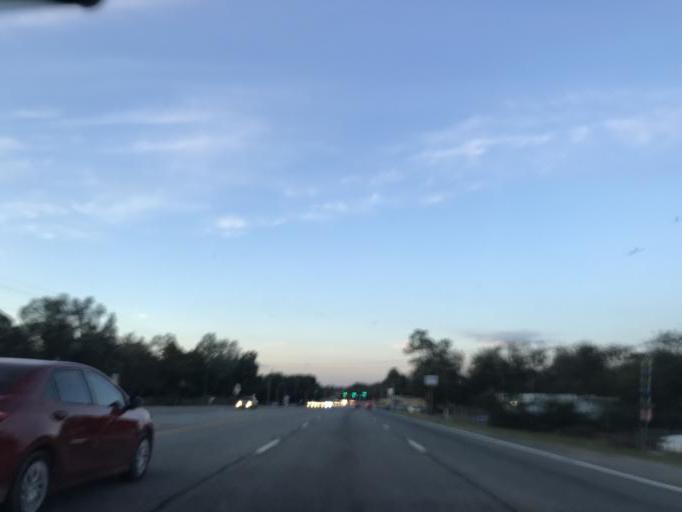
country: US
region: Georgia
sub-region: Bibb County
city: Macon
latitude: 32.7386
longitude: -83.6557
